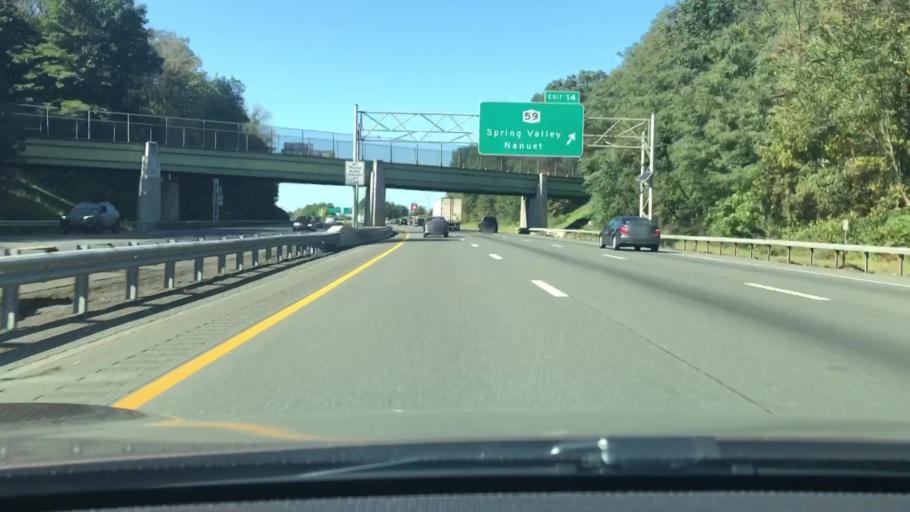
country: US
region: New York
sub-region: Rockland County
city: Nanuet
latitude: 41.1040
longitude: -74.0179
